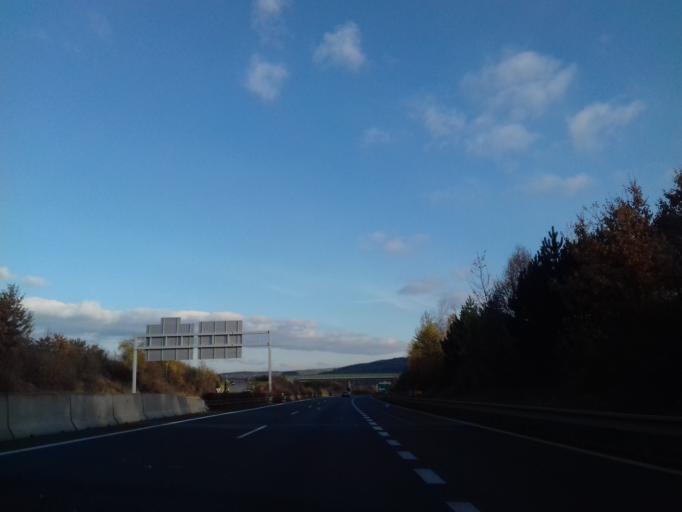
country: CZ
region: Plzensky
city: Stenovice
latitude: 49.6859
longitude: 13.3734
